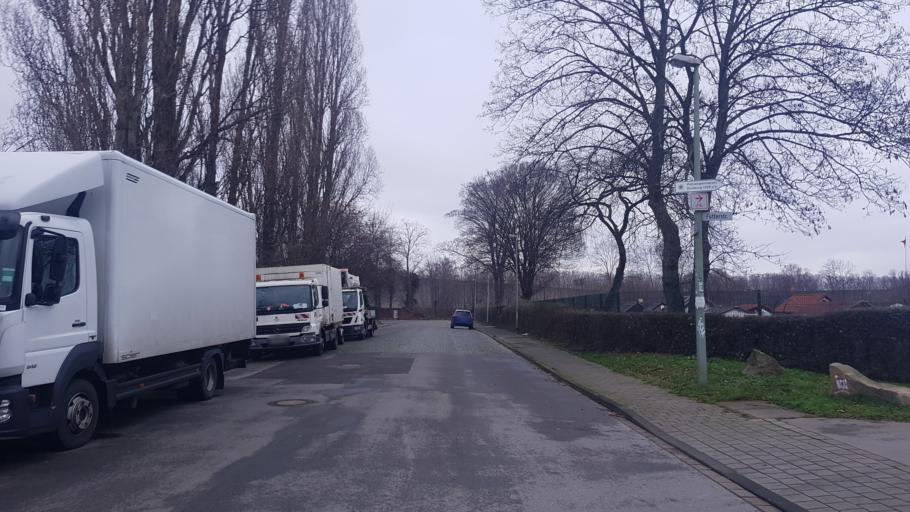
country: DE
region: North Rhine-Westphalia
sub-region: Regierungsbezirk Dusseldorf
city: Duisburg
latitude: 51.4446
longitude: 6.7817
